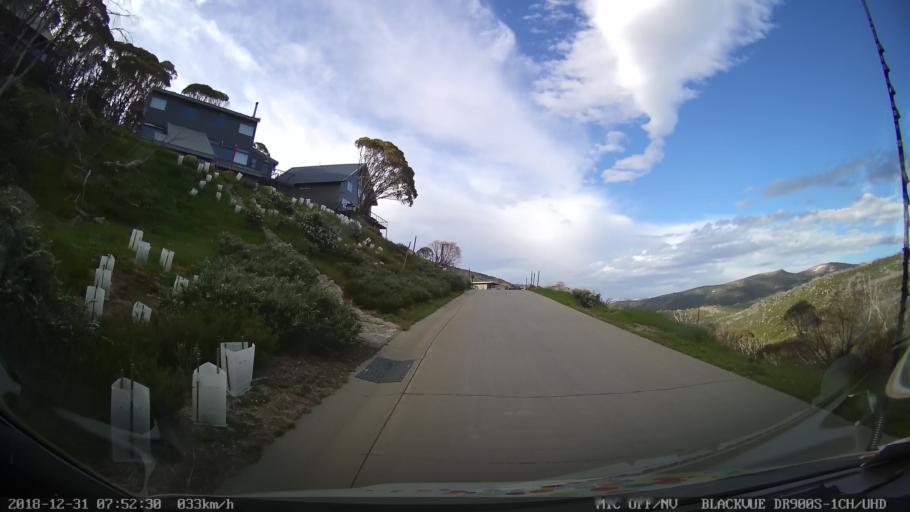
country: AU
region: New South Wales
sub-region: Snowy River
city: Jindabyne
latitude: -36.3812
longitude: 148.3731
